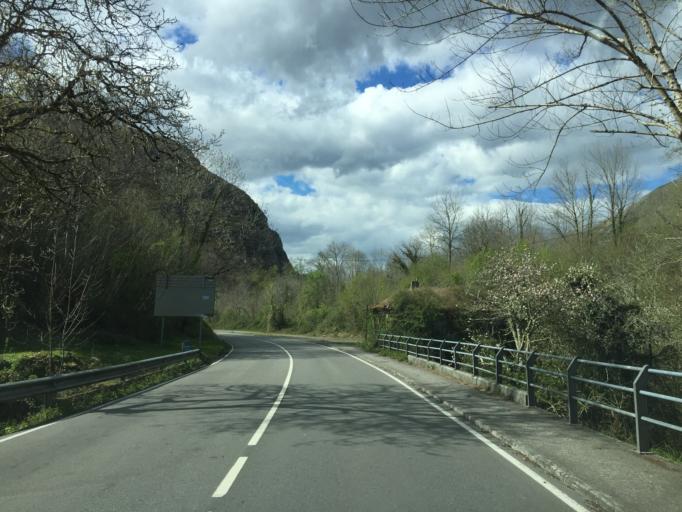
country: ES
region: Asturias
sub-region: Province of Asturias
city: Cangas de Onis
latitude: 43.3162
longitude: -5.0710
